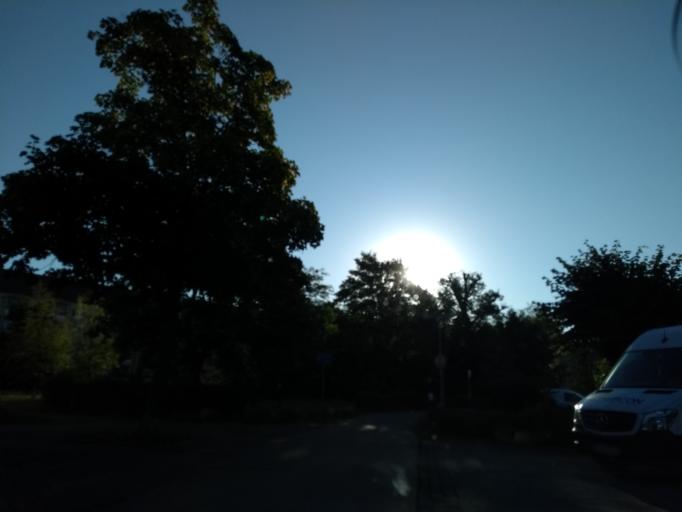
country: DE
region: Brandenburg
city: Lubbenau
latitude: 51.8586
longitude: 13.9531
